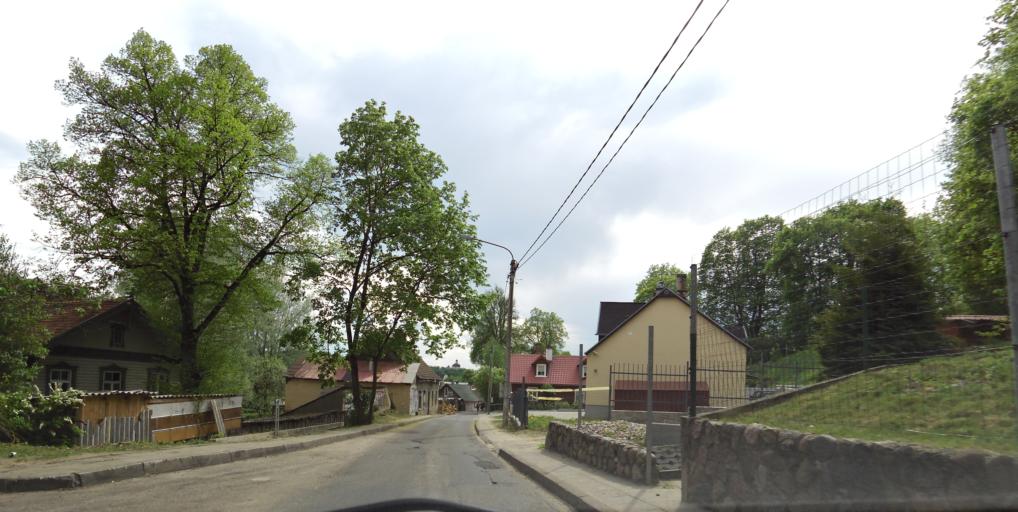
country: LT
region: Vilnius County
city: Rasos
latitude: 54.6845
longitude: 25.3038
